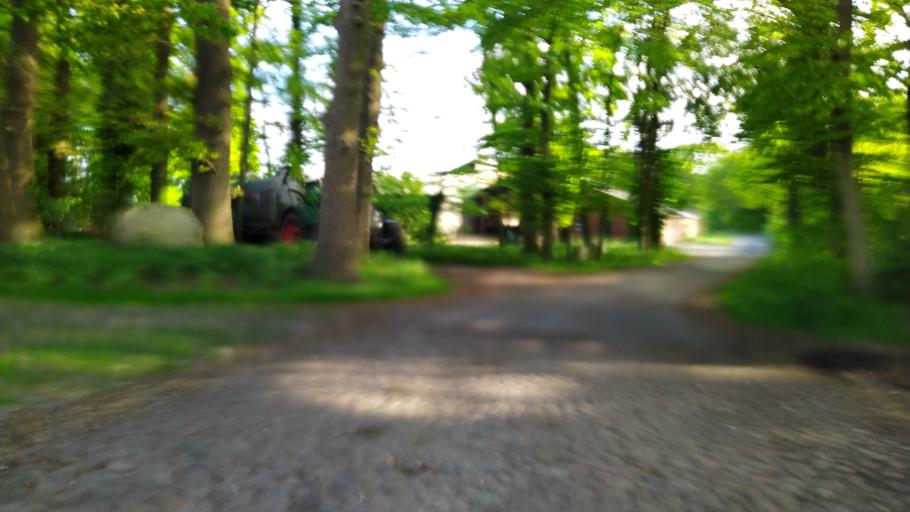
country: DE
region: Lower Saxony
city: Brest
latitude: 53.4003
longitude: 9.3613
